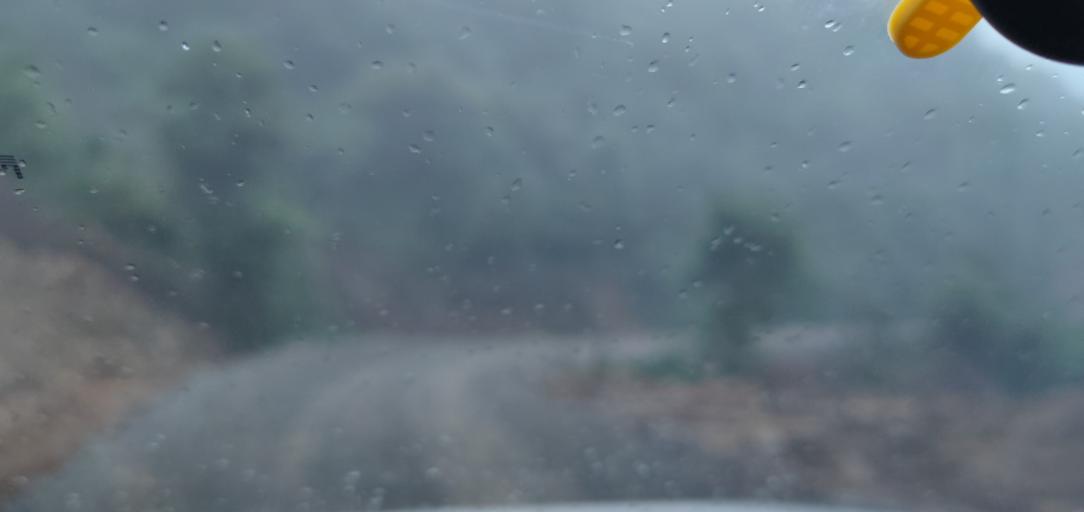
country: LA
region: Phongsali
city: Phongsali
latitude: 21.4203
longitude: 102.2511
